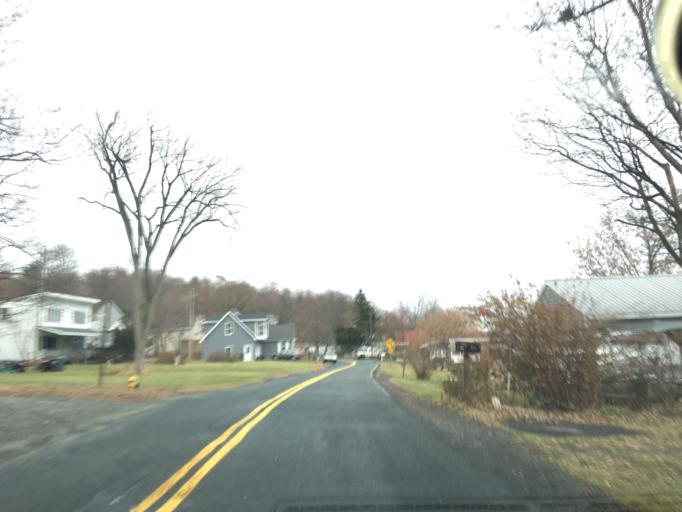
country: US
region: New York
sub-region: Rensselaer County
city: Wynantskill
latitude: 42.6617
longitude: -73.6405
